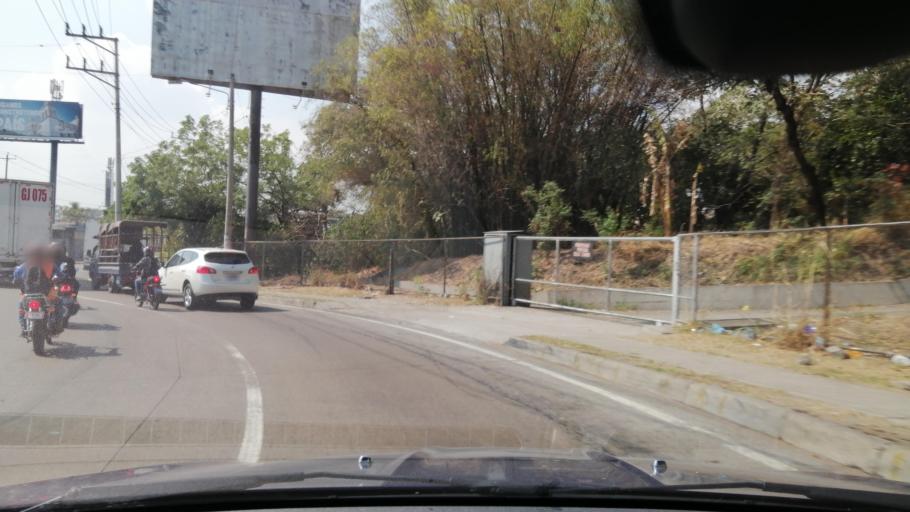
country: SV
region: San Salvador
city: Mejicanos
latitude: 13.7367
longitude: -89.2180
